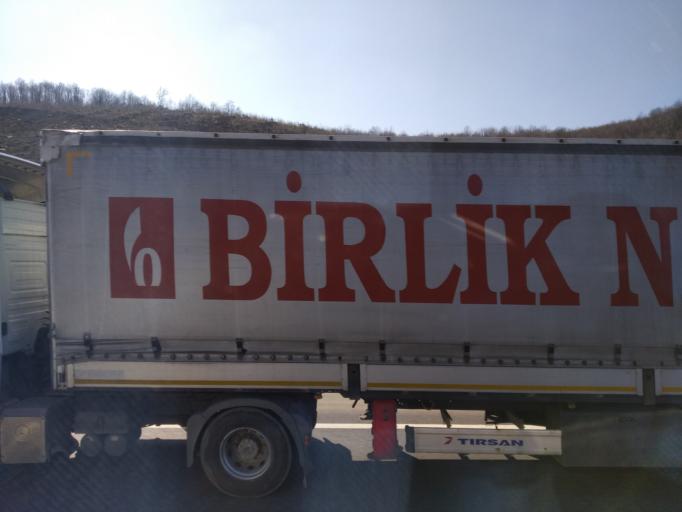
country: TR
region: Istanbul
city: Mahmut Sevket Pasa
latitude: 41.1595
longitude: 29.2612
